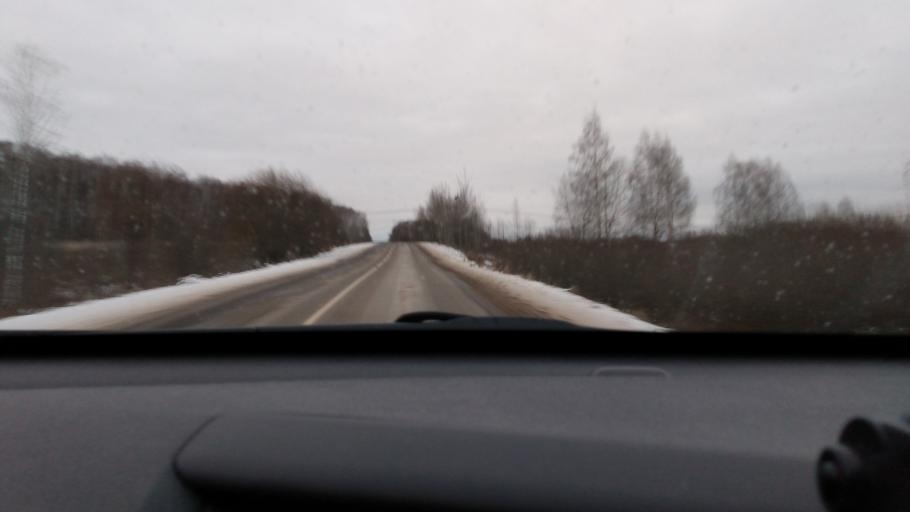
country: RU
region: Moskovskaya
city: Bronnitsy
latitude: 55.2901
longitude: 38.2517
